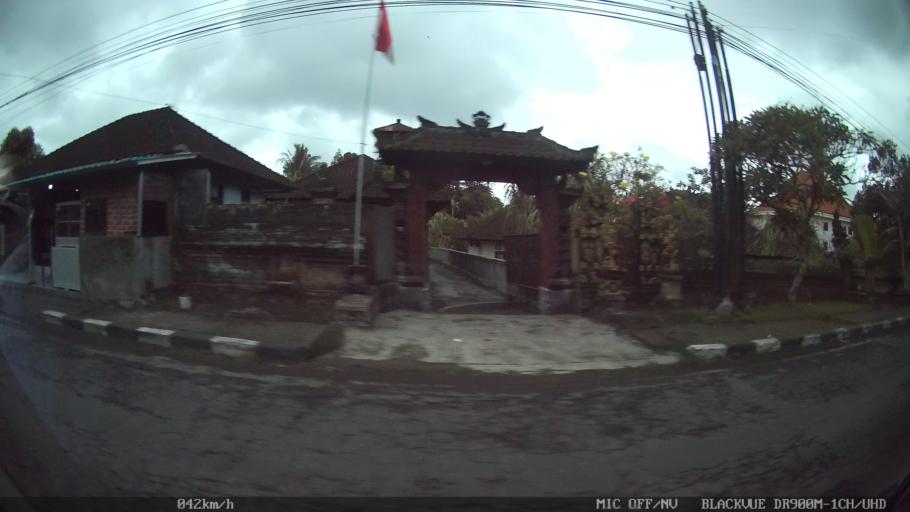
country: ID
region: Bali
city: Banjar Sempidi
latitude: -8.5244
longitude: 115.2060
